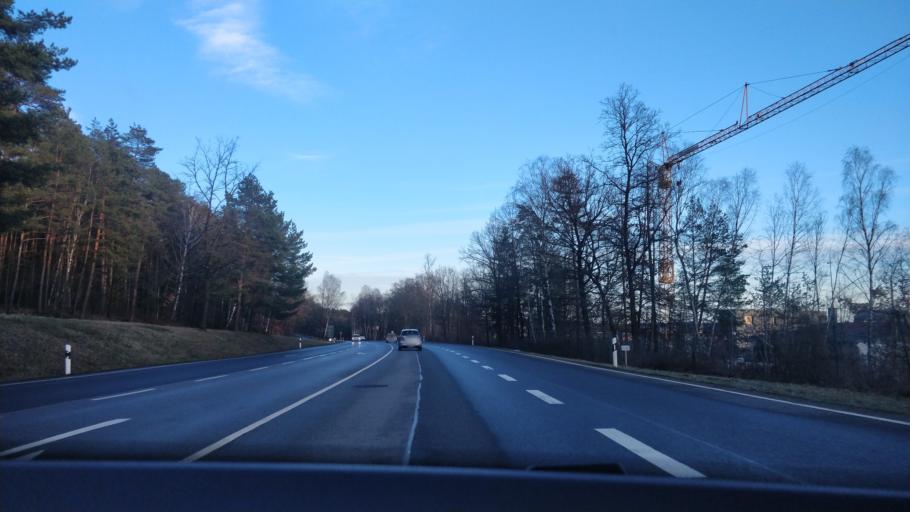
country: DE
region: Bavaria
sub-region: Upper Palatinate
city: Parkstein
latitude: 49.6905
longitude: 12.0940
